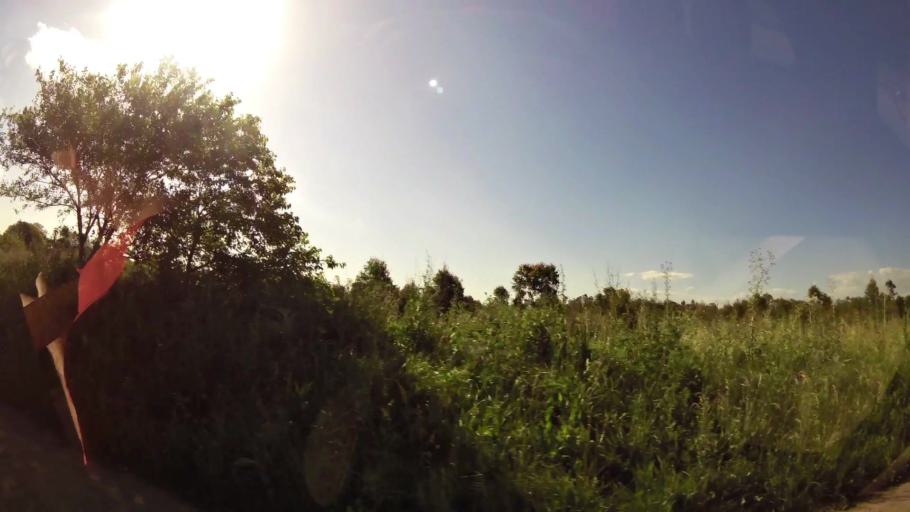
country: UY
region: Canelones
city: La Paz
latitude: -34.8117
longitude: -56.1674
